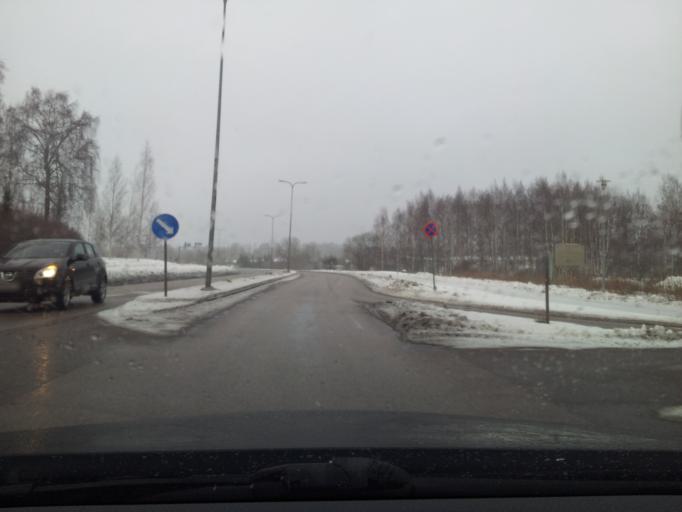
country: FI
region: Uusimaa
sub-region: Helsinki
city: Koukkuniemi
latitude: 60.1798
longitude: 24.7790
